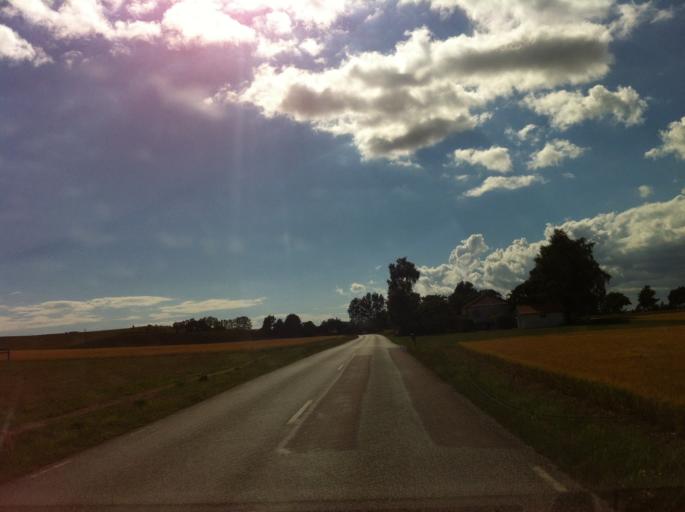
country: SE
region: Skane
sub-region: Ystads Kommun
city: Kopingebro
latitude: 55.3965
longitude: 14.0347
